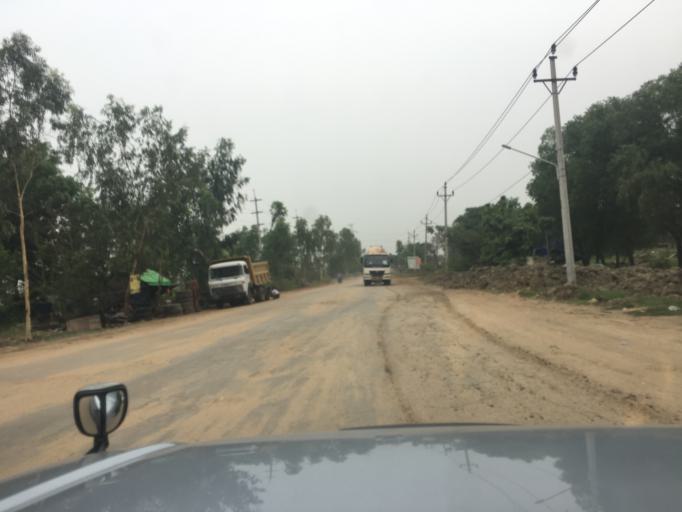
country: MM
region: Yangon
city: Syriam
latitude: 16.9474
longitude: 96.2812
